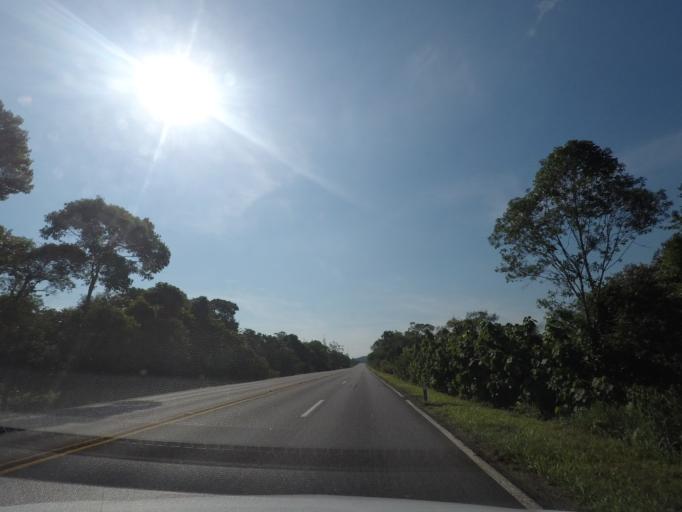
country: BR
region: Parana
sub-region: Paranagua
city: Paranagua
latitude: -25.5893
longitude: -48.6114
